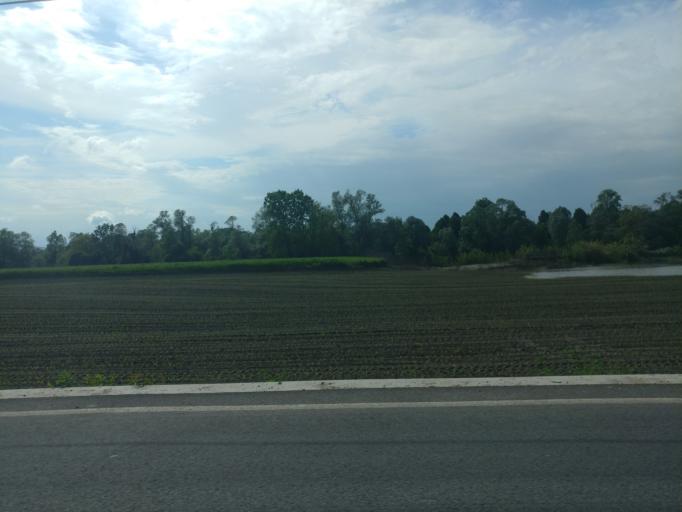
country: IT
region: Piedmont
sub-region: Provincia di Cuneo
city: Faule
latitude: 44.8144
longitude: 7.5856
